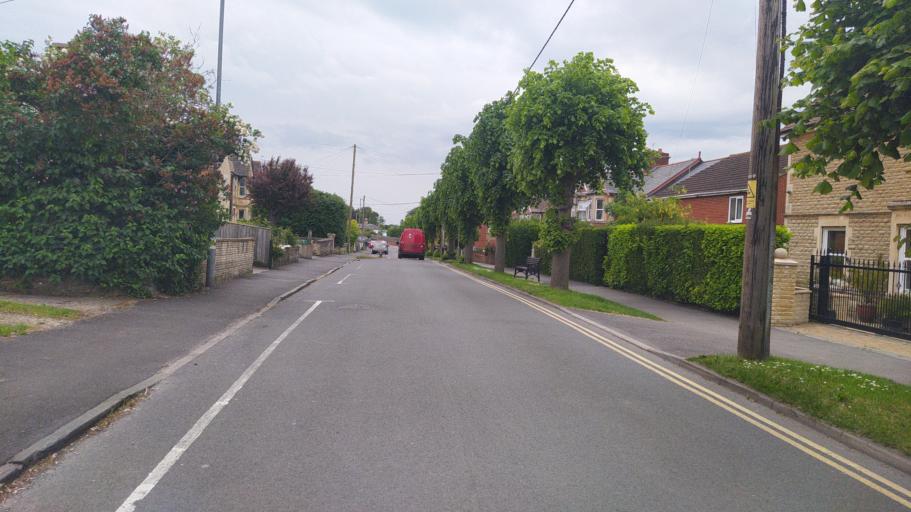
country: GB
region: England
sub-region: Wiltshire
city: Melksham
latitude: 51.3790
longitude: -2.1310
